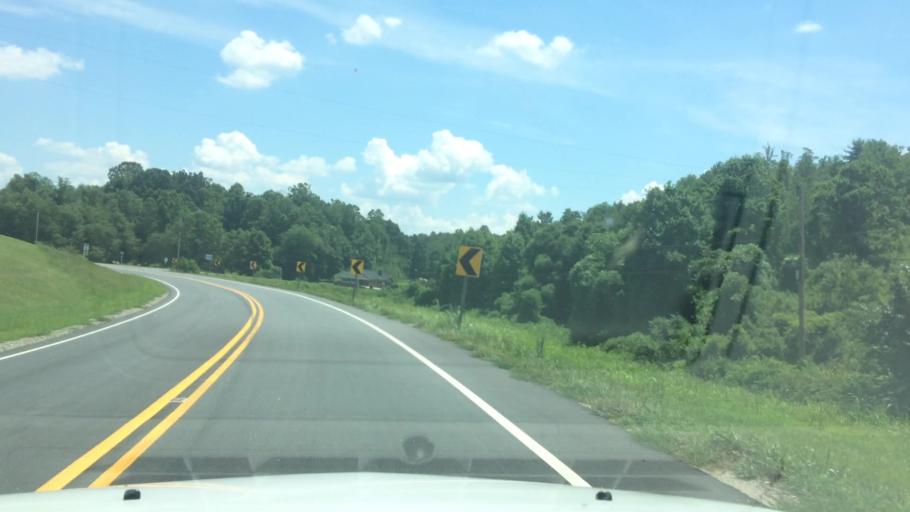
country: US
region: North Carolina
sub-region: Alexander County
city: Taylorsville
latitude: 35.9190
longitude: -81.2544
